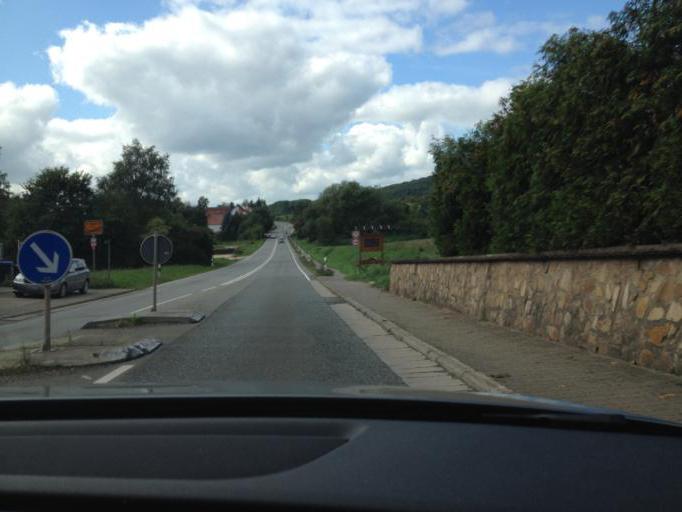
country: DE
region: Saarland
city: Namborn
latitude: 49.5270
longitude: 7.1685
